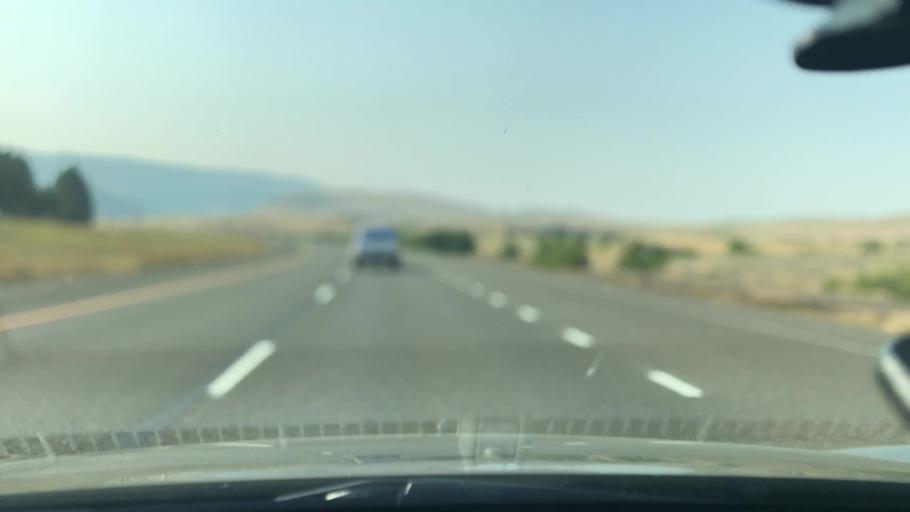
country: US
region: Oregon
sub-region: Union County
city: Union
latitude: 45.1859
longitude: -117.9898
